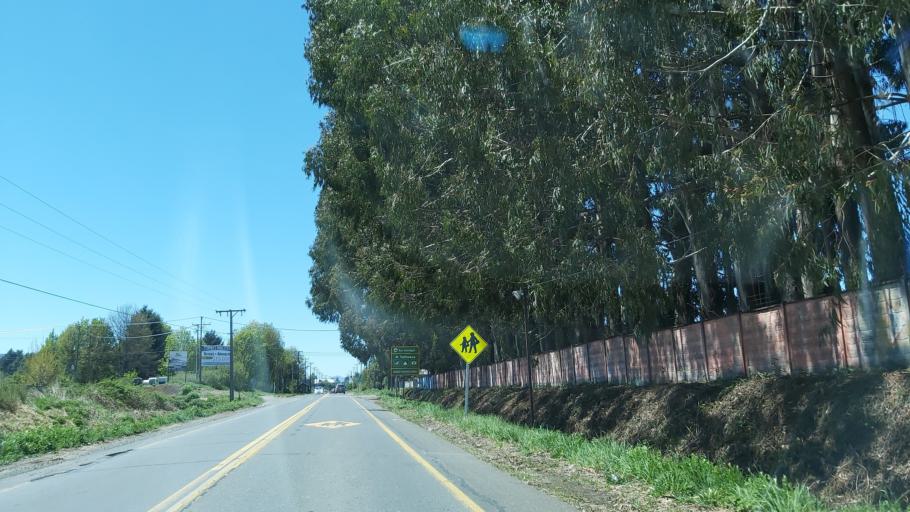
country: CL
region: Araucania
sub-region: Provincia de Cautin
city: Vilcun
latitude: -38.4343
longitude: -71.9038
